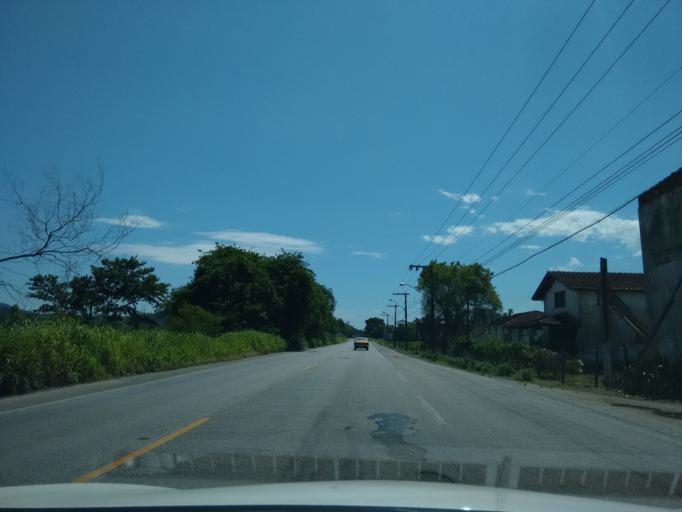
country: BR
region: Santa Catarina
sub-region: Itajai
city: Itajai
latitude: -26.8826
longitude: -48.8008
